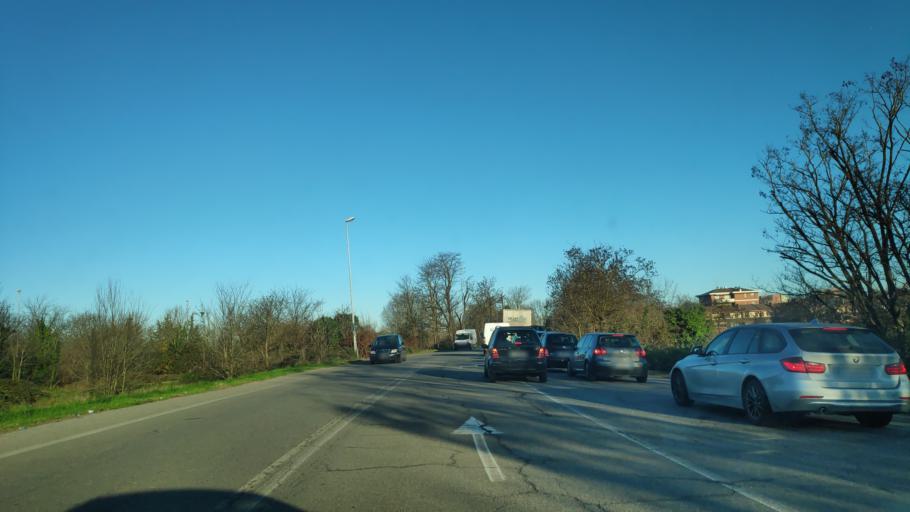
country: IT
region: Lombardy
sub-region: Citta metropolitana di Milano
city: Fizzonasco
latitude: 45.3650
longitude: 9.1899
